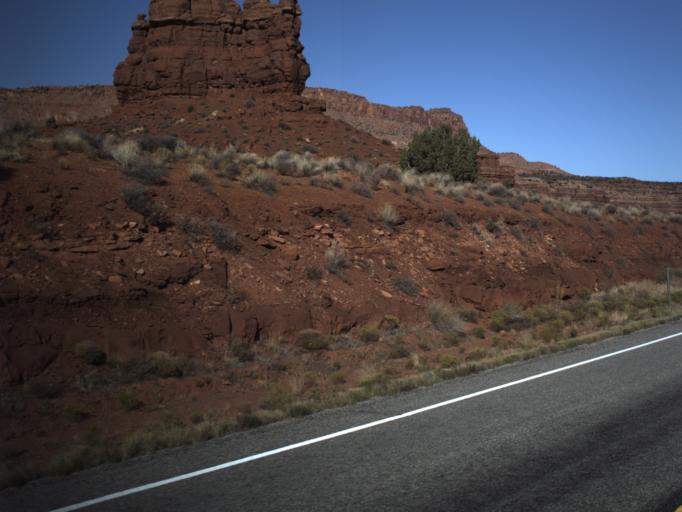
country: US
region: Utah
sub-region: San Juan County
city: Blanding
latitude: 37.6991
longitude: -110.2318
